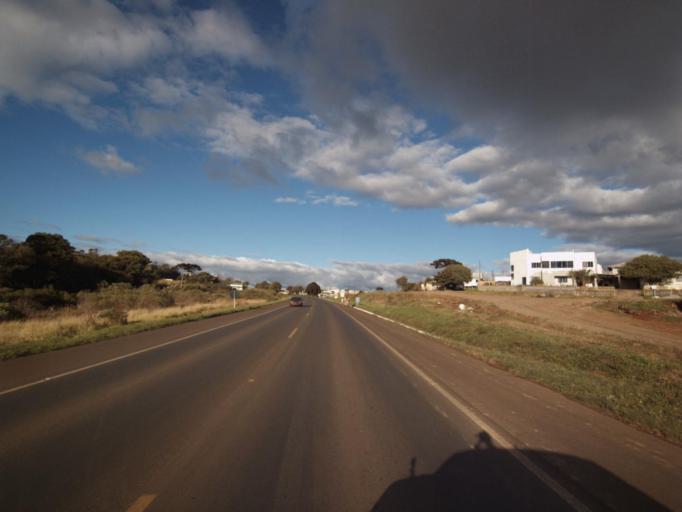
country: BR
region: Santa Catarina
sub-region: Campos Novos
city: Campos Novos
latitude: -27.3904
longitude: -51.2230
